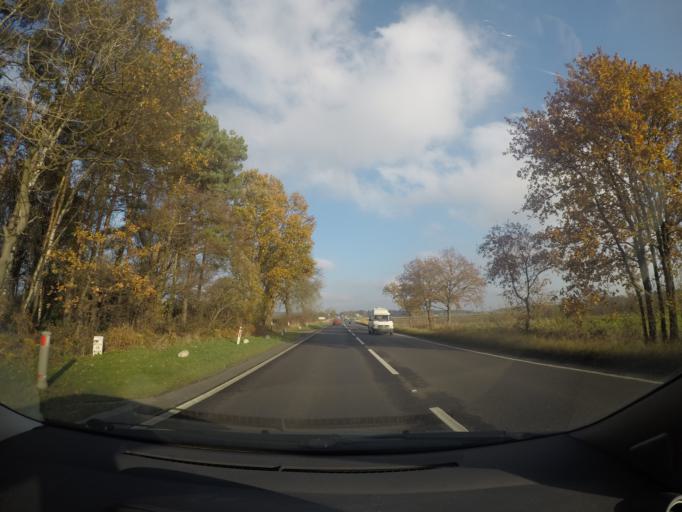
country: GB
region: England
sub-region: City of York
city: Murton
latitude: 54.0072
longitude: -1.0033
